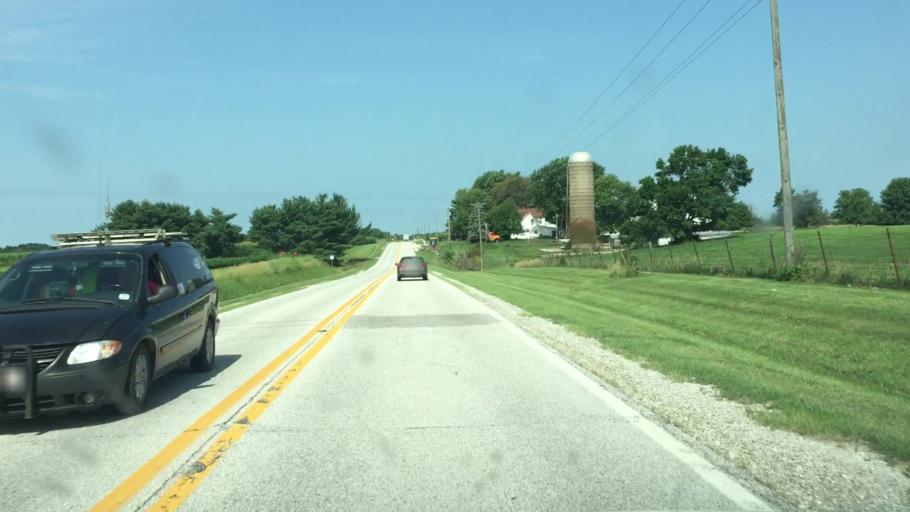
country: US
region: Illinois
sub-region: Hancock County
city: Nauvoo
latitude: 40.5519
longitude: -91.3370
